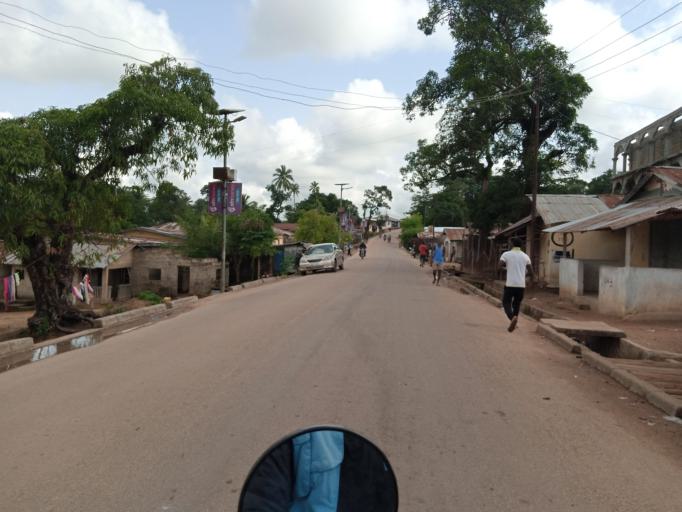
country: SL
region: Southern Province
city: Bo
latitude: 7.9746
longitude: -11.7389
